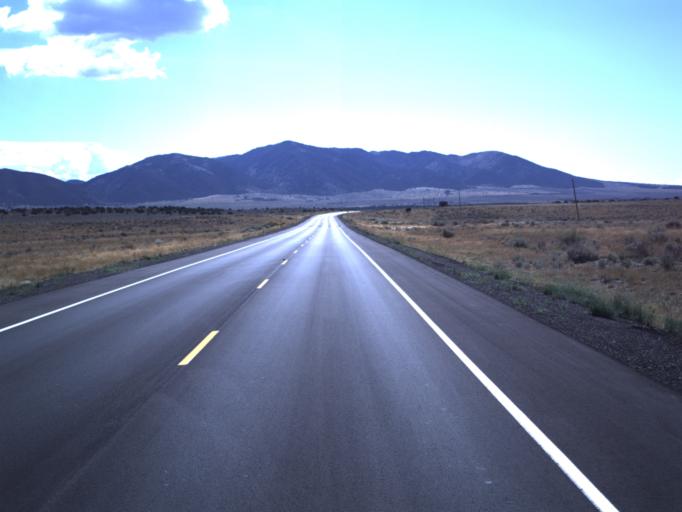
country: US
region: Utah
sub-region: Utah County
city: Eagle Mountain
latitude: 40.0572
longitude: -112.3060
